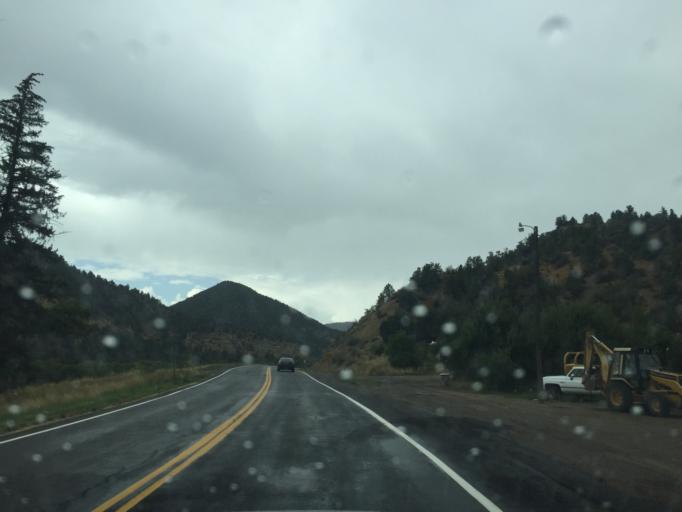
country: US
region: Utah
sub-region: Kane County
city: Kanab
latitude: 37.3229
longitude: -112.5978
